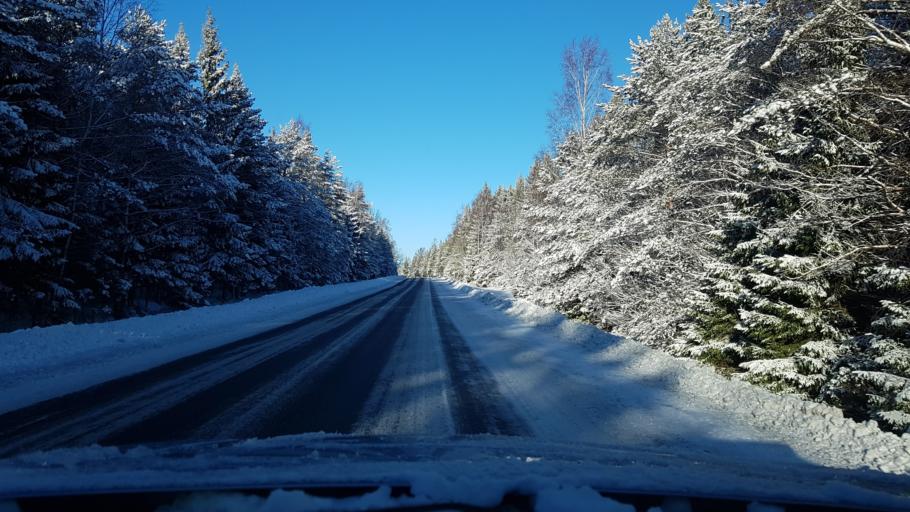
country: EE
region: Hiiumaa
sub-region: Kaerdla linn
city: Kardla
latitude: 58.9734
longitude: 22.8218
